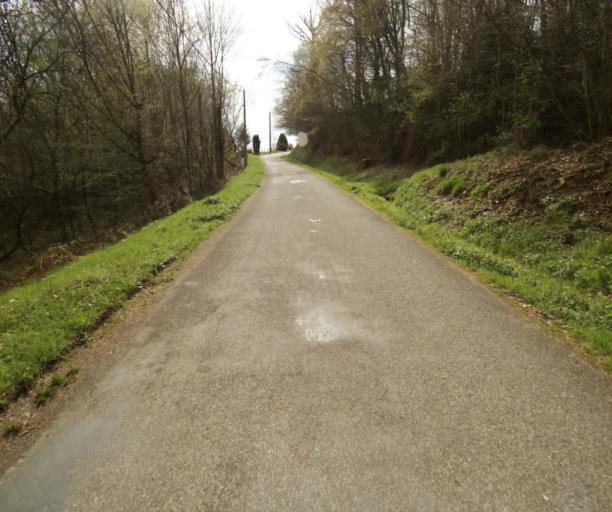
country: FR
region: Limousin
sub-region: Departement de la Correze
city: Laguenne
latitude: 45.2372
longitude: 1.8404
